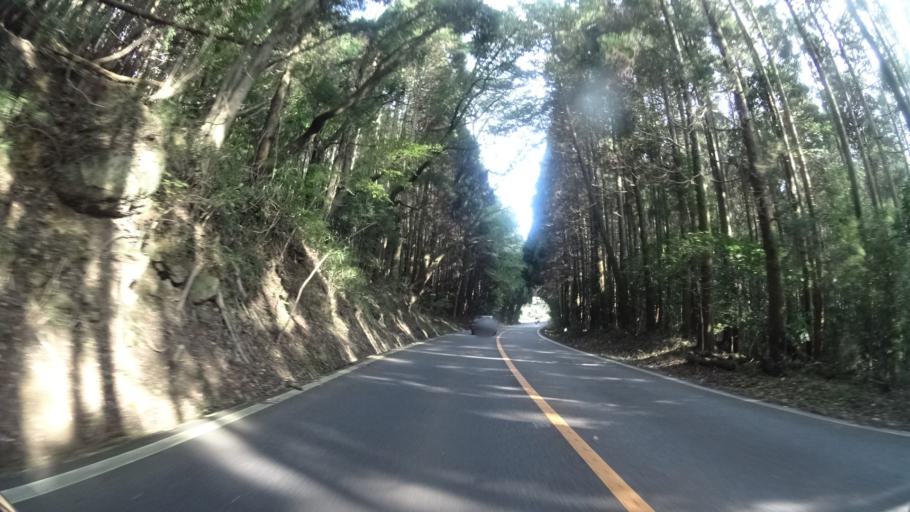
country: JP
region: Oita
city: Beppu
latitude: 33.2633
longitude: 131.3744
